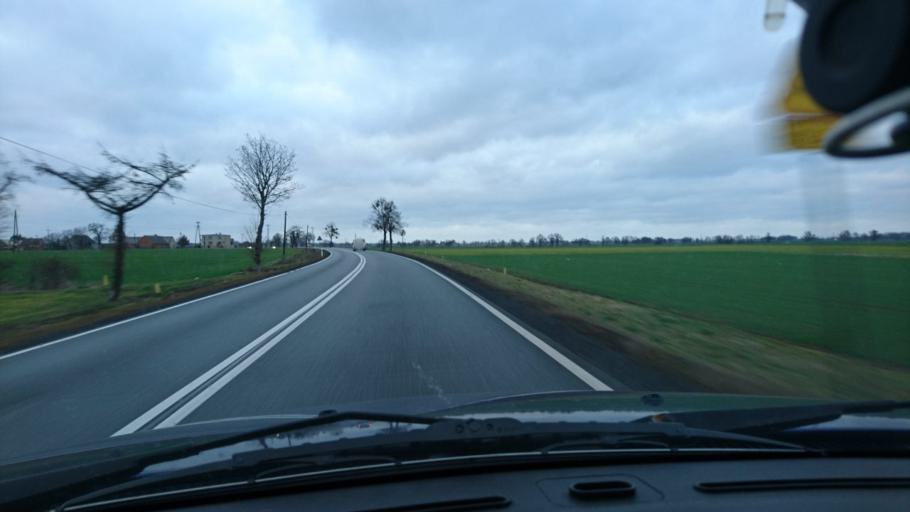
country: PL
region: Opole Voivodeship
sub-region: Powiat kluczborski
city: Kluczbork
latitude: 51.0093
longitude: 18.2044
